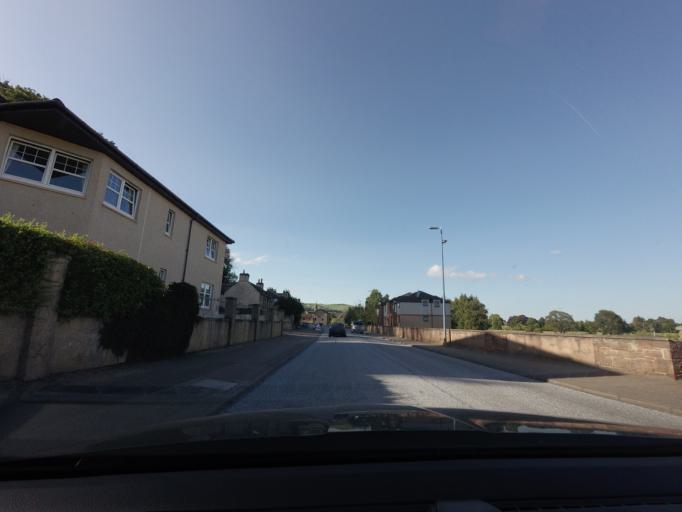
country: GB
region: Scotland
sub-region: Highland
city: Dingwall
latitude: 57.5911
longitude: -4.4240
